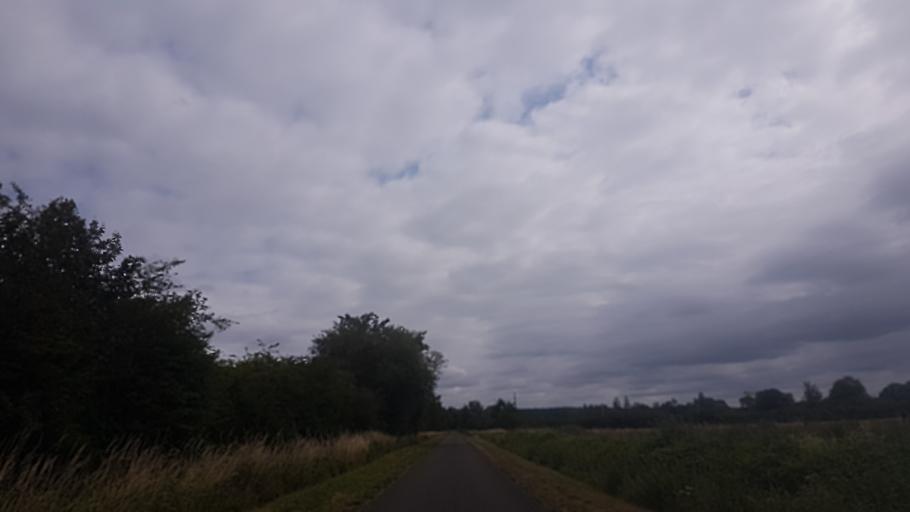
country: BE
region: Wallonia
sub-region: Province de Namur
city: Couvin
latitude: 50.1018
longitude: 4.5448
